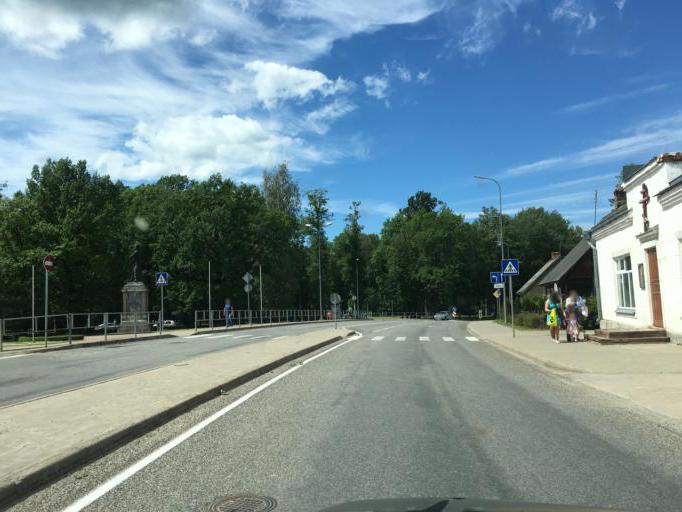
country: LV
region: Balvu Rajons
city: Balvi
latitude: 57.1327
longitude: 27.2645
